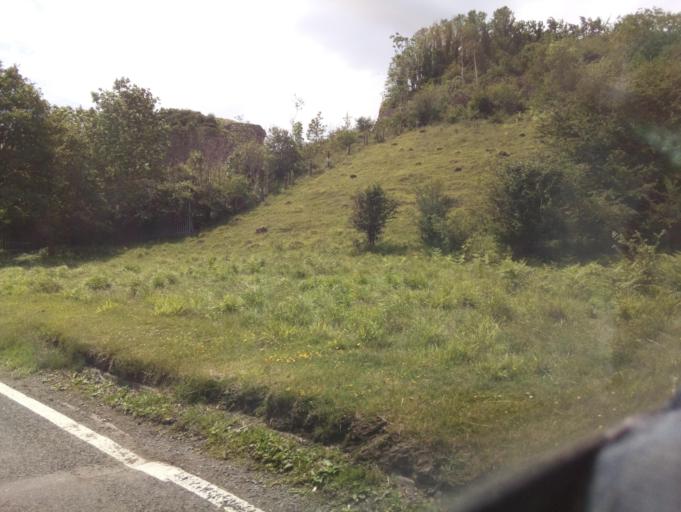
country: GB
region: Wales
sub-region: Bridgend county borough
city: Merthyr Mawr
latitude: 51.4727
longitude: -3.5897
